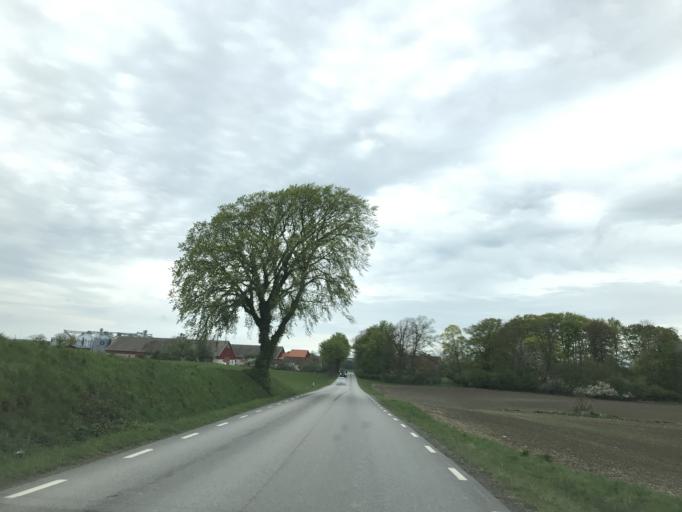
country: SE
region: Skane
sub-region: Trelleborgs Kommun
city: Anderslov
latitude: 55.4876
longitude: 13.3398
